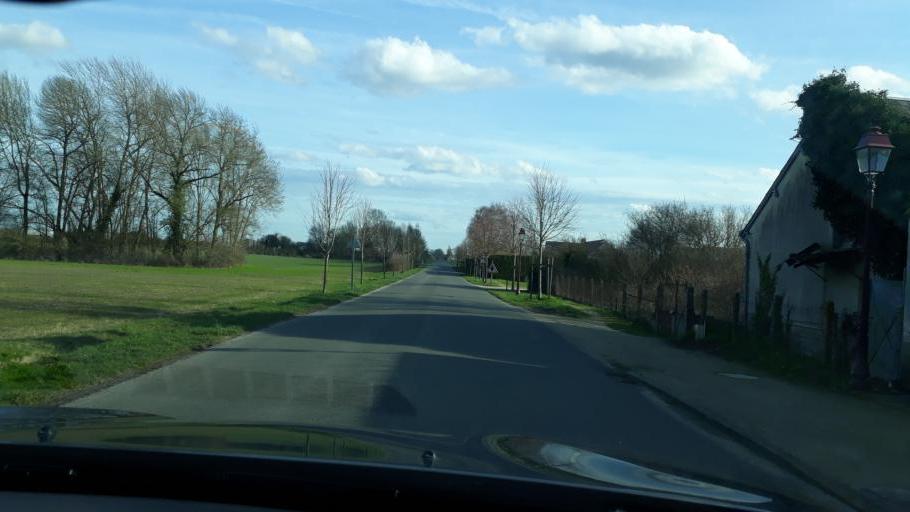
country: FR
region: Centre
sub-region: Departement du Loiret
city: Chilleurs-aux-Bois
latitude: 48.0716
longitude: 2.1372
